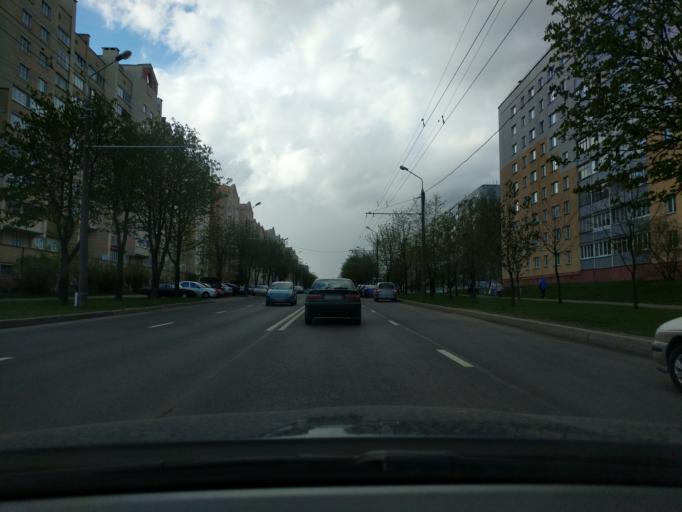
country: BY
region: Minsk
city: Novoye Medvezhino
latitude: 53.9031
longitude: 27.4816
